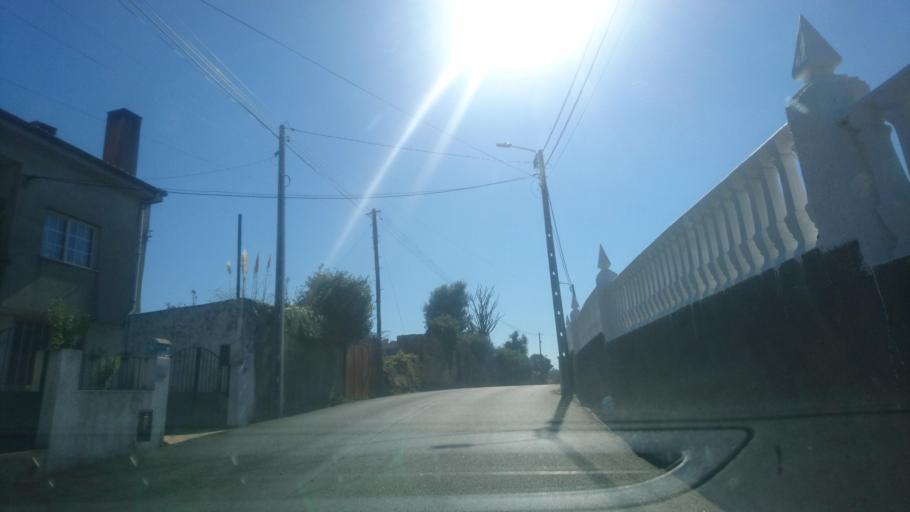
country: PT
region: Aveiro
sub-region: Santa Maria da Feira
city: Lamas
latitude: 40.9872
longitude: -8.5721
